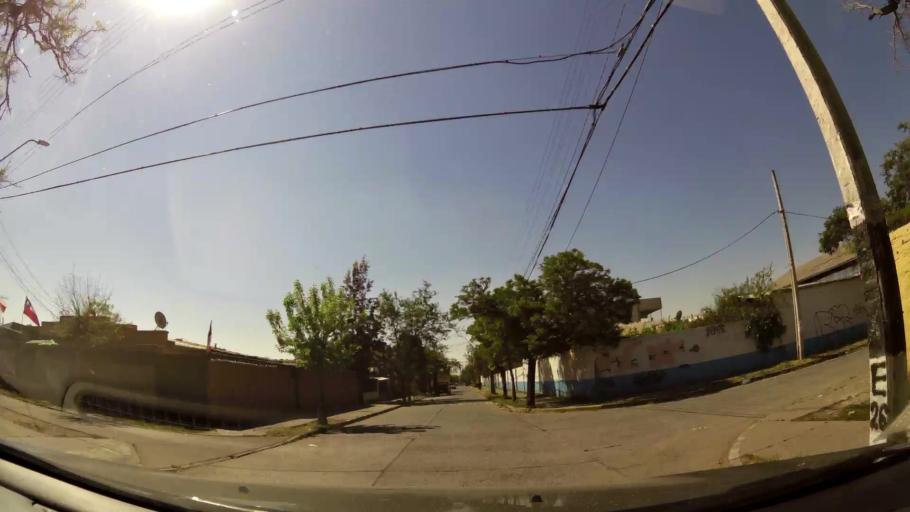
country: CL
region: Santiago Metropolitan
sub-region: Provincia de Maipo
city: San Bernardo
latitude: -33.5820
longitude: -70.7066
